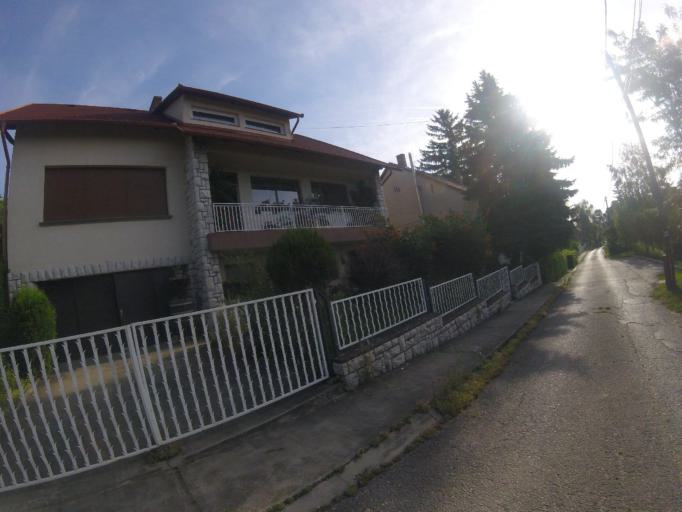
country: HU
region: Baranya
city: Villany
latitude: 45.8746
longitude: 18.4521
